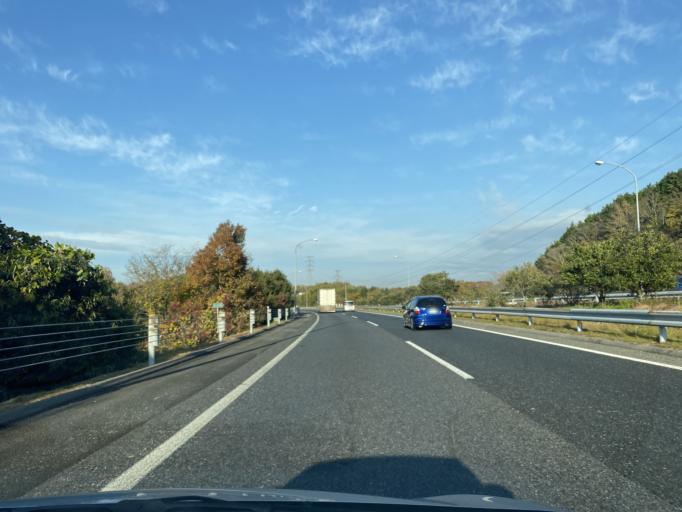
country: JP
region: Osaka
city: Izumi
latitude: 34.4085
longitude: 135.4470
